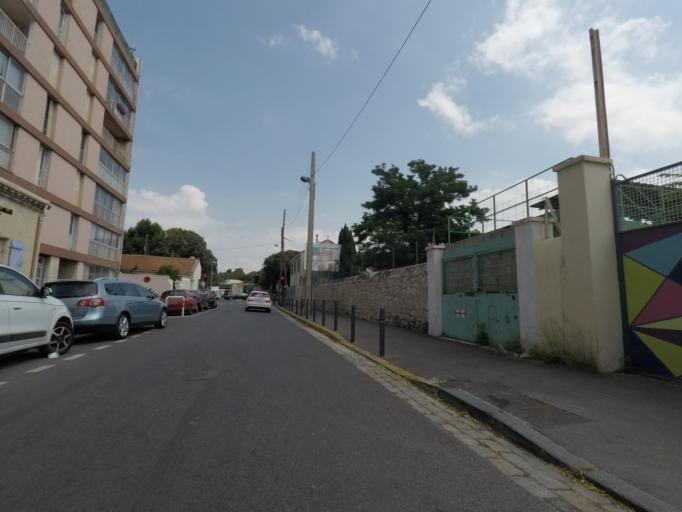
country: FR
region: Provence-Alpes-Cote d'Azur
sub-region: Departement des Bouches-du-Rhone
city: Marseille 10
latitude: 43.2828
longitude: 5.4128
